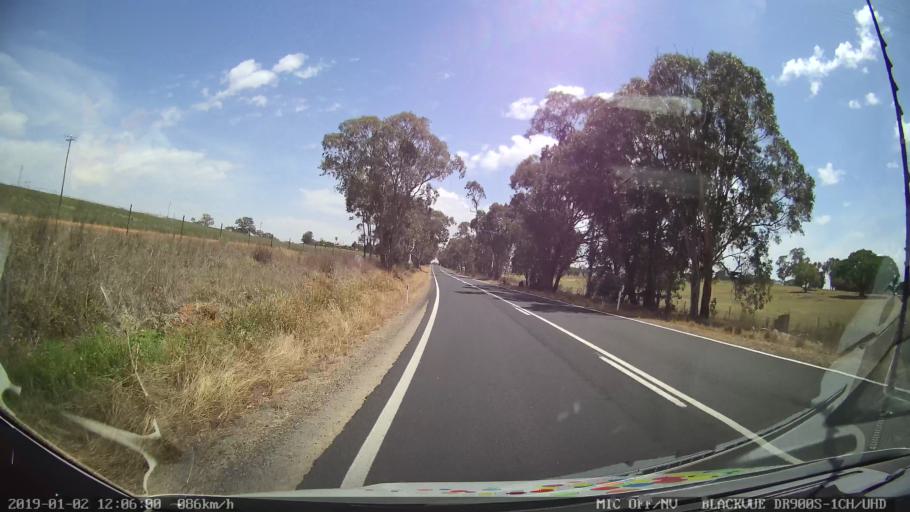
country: AU
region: New South Wales
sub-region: Young
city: Young
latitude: -34.5078
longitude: 148.2982
